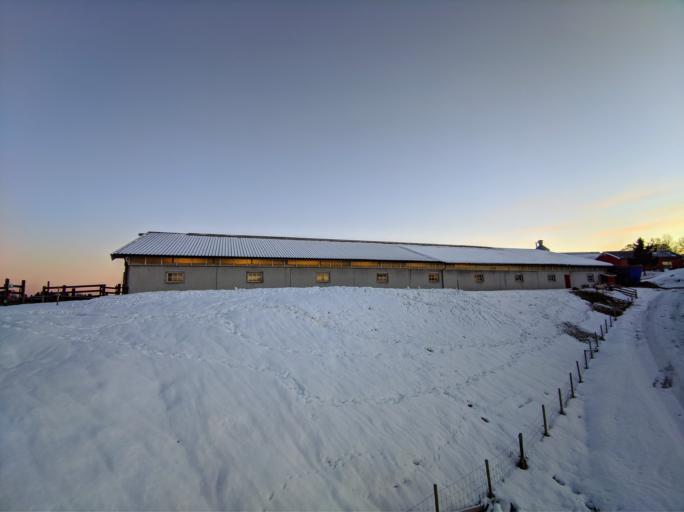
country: NO
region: Akershus
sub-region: Nannestad
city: Teigebyen
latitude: 60.1703
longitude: 11.0583
